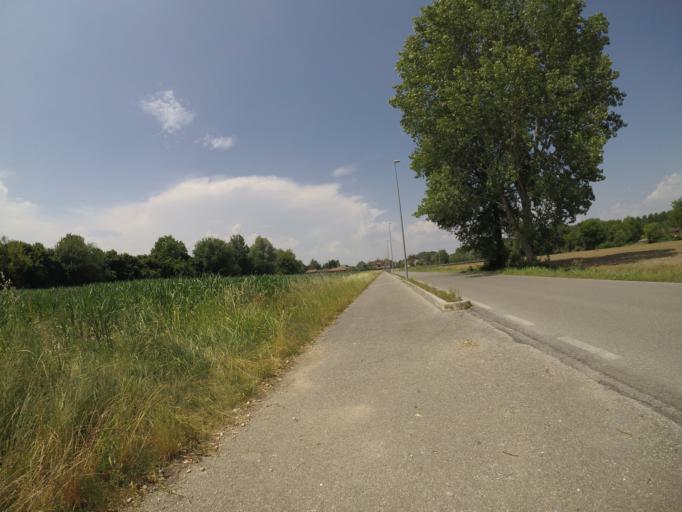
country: IT
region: Friuli Venezia Giulia
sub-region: Provincia di Udine
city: Rivignano
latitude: 45.8790
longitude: 13.0509
